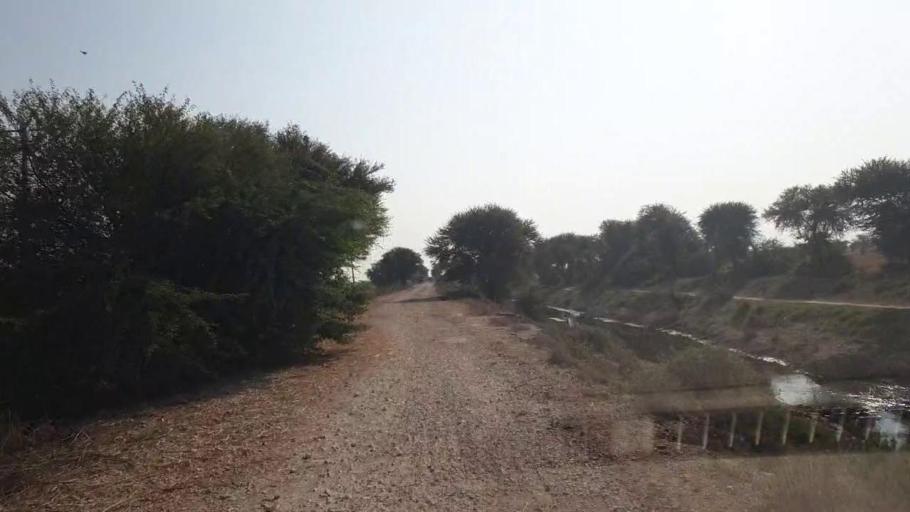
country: PK
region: Sindh
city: Kario
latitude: 24.9097
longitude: 68.6494
